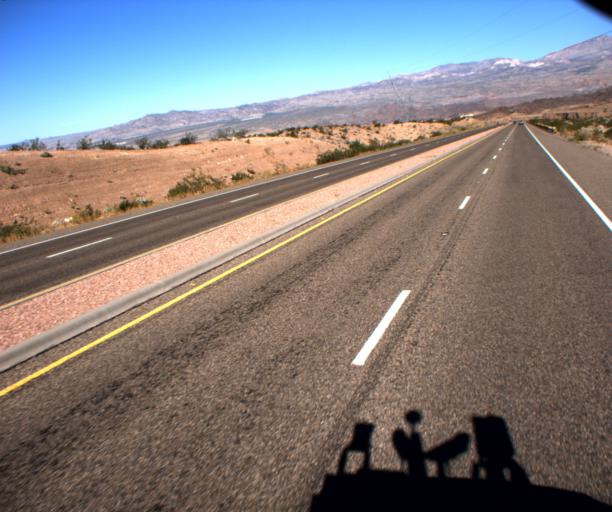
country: US
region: Nevada
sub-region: Clark County
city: Laughlin
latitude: 35.1890
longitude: -114.5104
